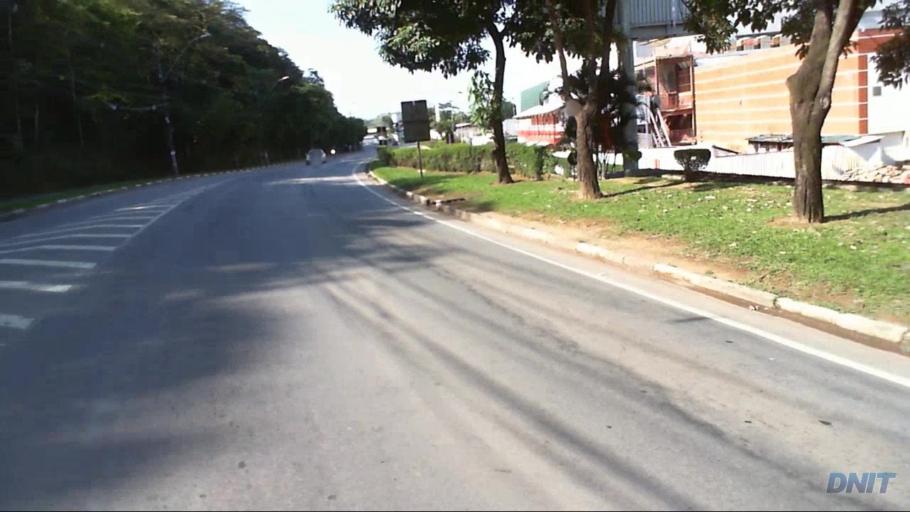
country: BR
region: Minas Gerais
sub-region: Ipatinga
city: Ipatinga
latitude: -19.4961
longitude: -42.5670
